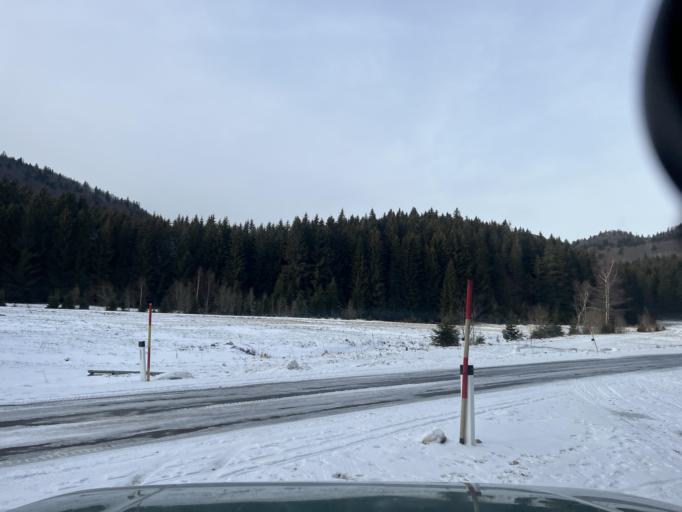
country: SI
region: Ajdovscina
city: Lokavec
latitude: 45.9789
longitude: 13.8253
